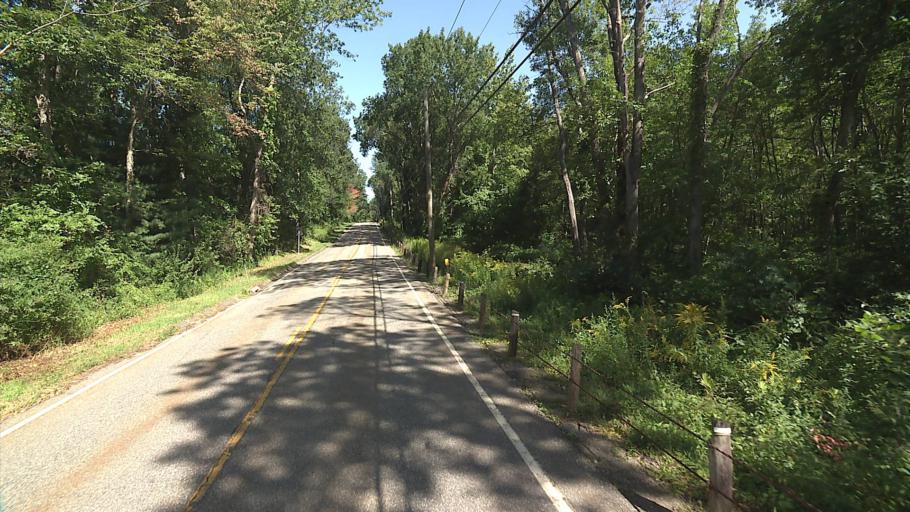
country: US
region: Connecticut
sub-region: Litchfield County
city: Northwest Harwinton
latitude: 41.7419
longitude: -73.0780
